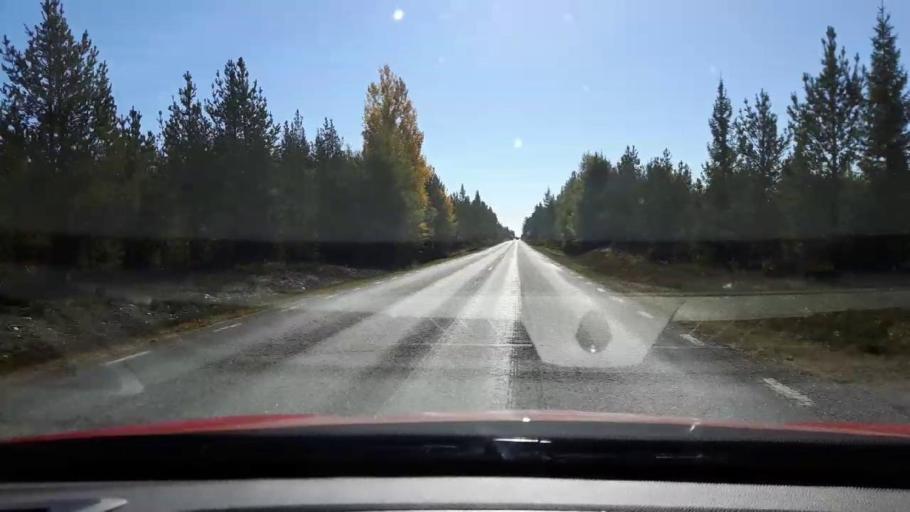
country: SE
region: Jaemtland
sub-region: Harjedalens Kommun
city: Sveg
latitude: 62.4175
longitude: 13.9119
